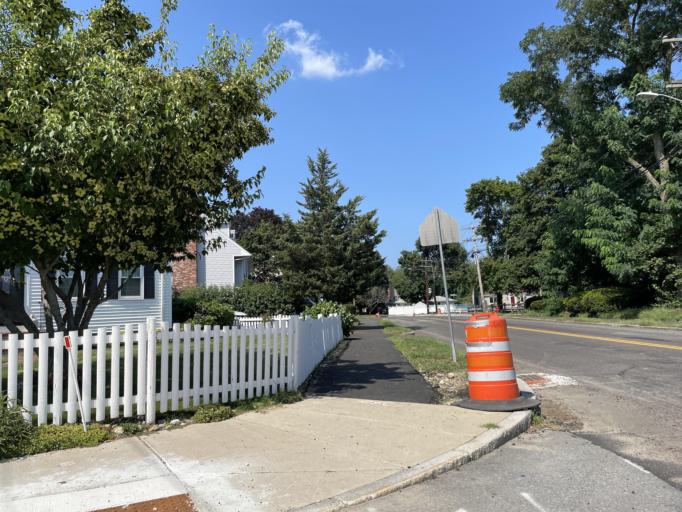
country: US
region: Massachusetts
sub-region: Middlesex County
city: Wakefield
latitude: 42.5203
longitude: -71.0636
